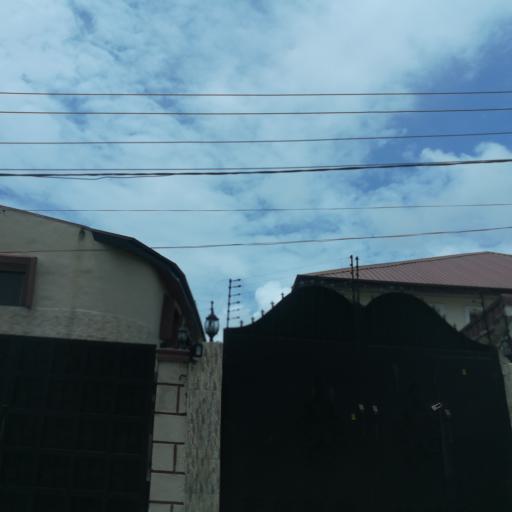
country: NG
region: Lagos
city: Ikoyi
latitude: 6.4391
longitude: 3.4650
